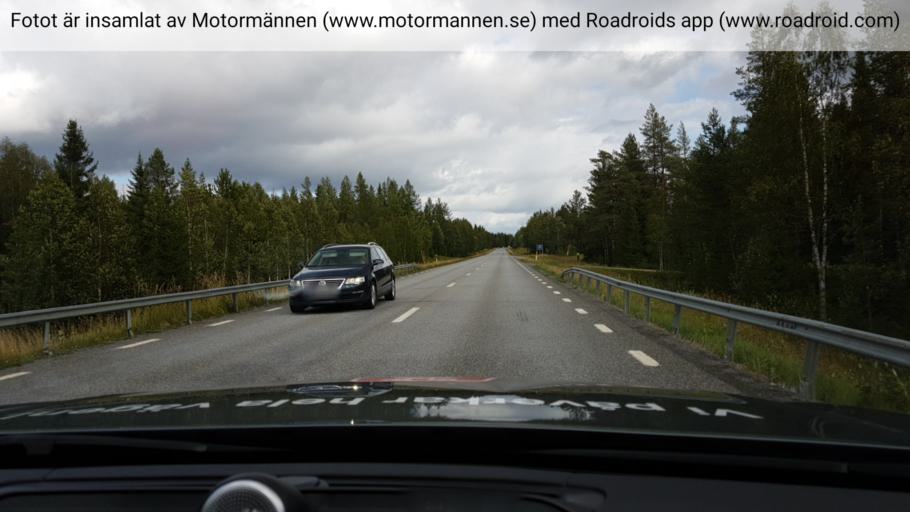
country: SE
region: Jaemtland
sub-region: OEstersunds Kommun
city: Lit
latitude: 63.4078
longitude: 15.0665
